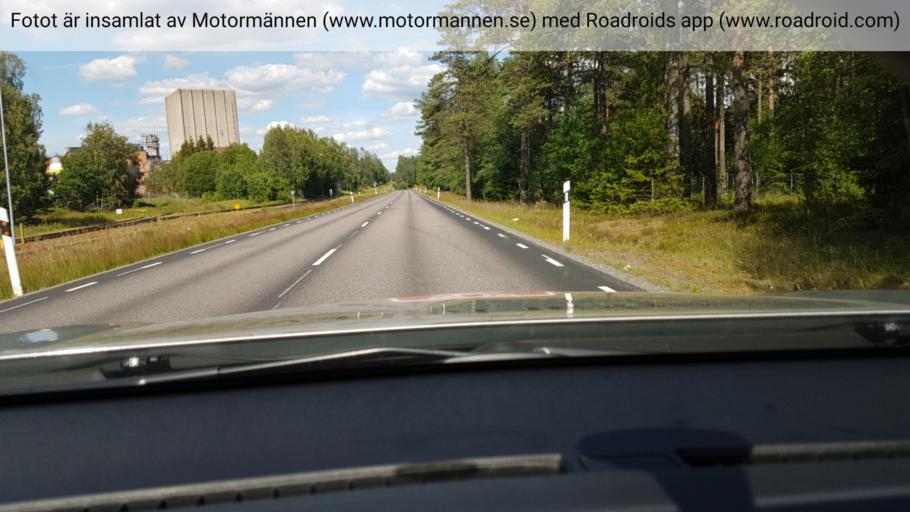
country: SE
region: Joenkoeping
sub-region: Vaggeryds Kommun
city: Vaggeryd
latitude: 57.4827
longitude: 14.1138
